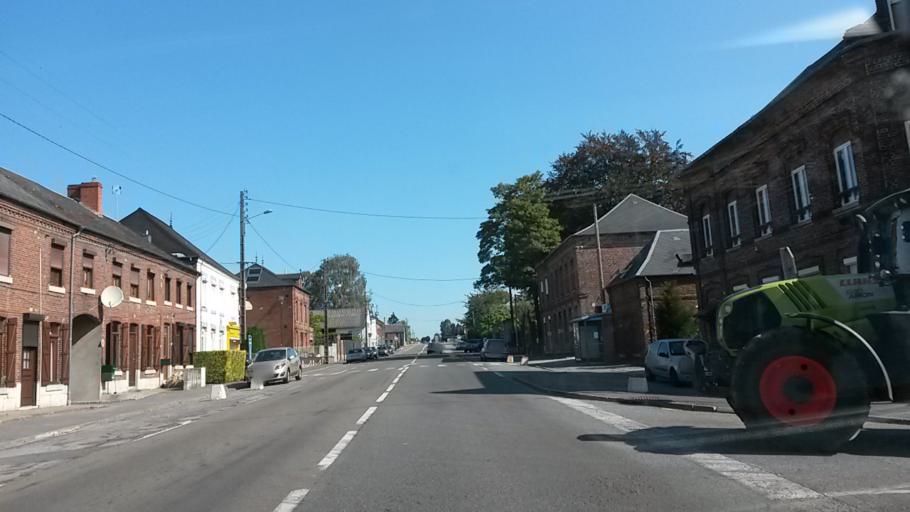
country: FR
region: Nord-Pas-de-Calais
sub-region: Departement du Nord
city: Avesnes-sur-Helpe
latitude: 50.1290
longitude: 3.9373
